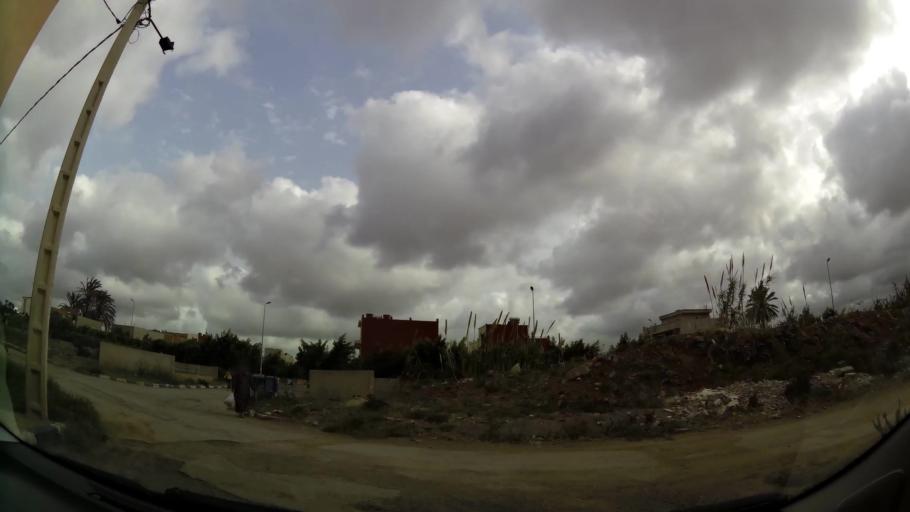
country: MA
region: Oriental
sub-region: Nador
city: Nador
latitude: 35.1601
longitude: -2.9187
